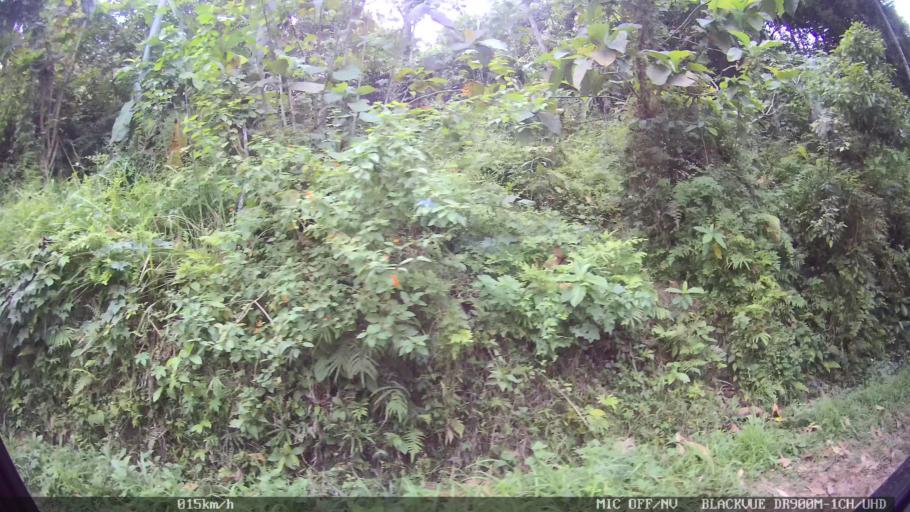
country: ID
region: Lampung
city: Bandarlampung
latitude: -5.4272
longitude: 105.3029
